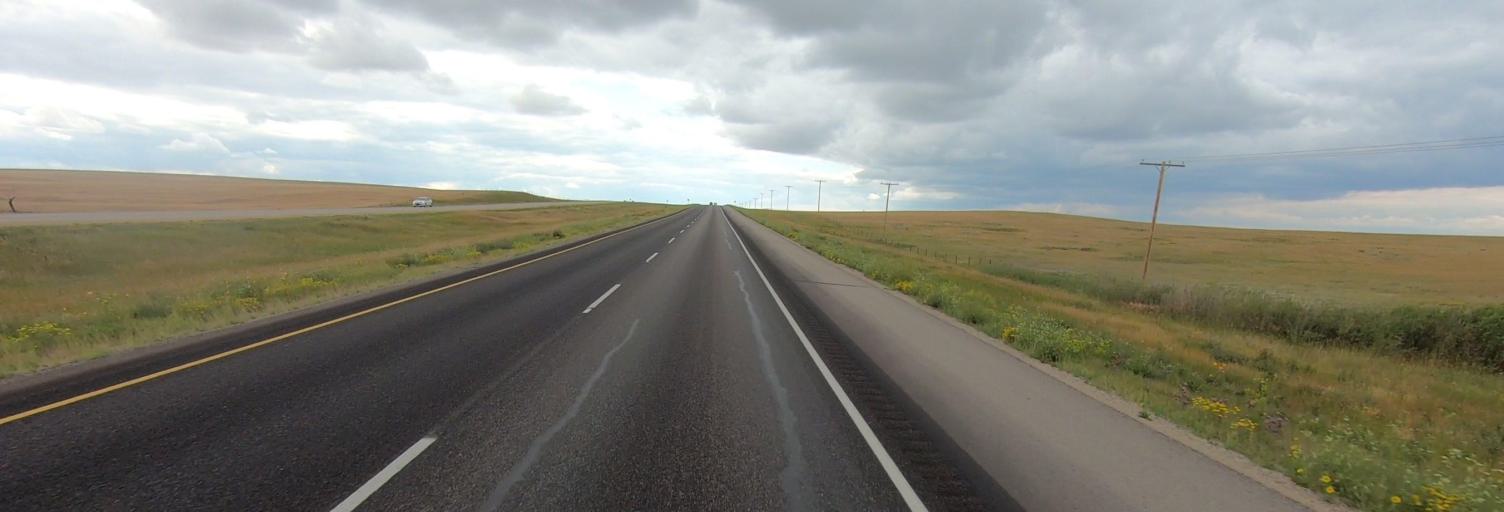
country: CA
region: Saskatchewan
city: Shaunavon
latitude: 50.0707
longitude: -108.6839
